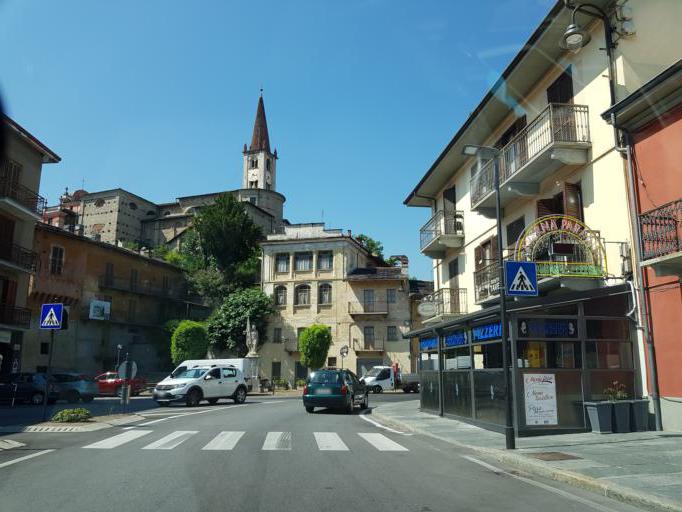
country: IT
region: Piedmont
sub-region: Provincia di Cuneo
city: Caraglio
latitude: 44.4192
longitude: 7.4326
